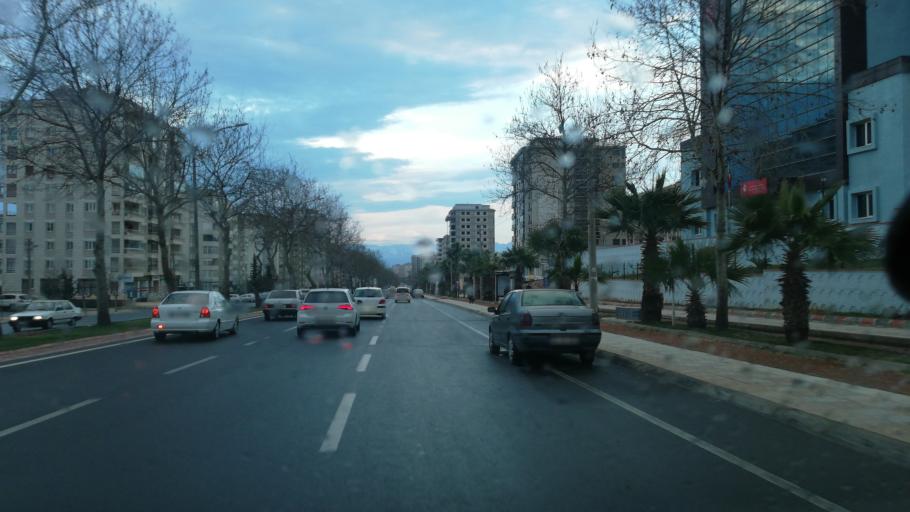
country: TR
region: Kahramanmaras
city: Kahramanmaras
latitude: 37.5894
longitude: 36.8773
